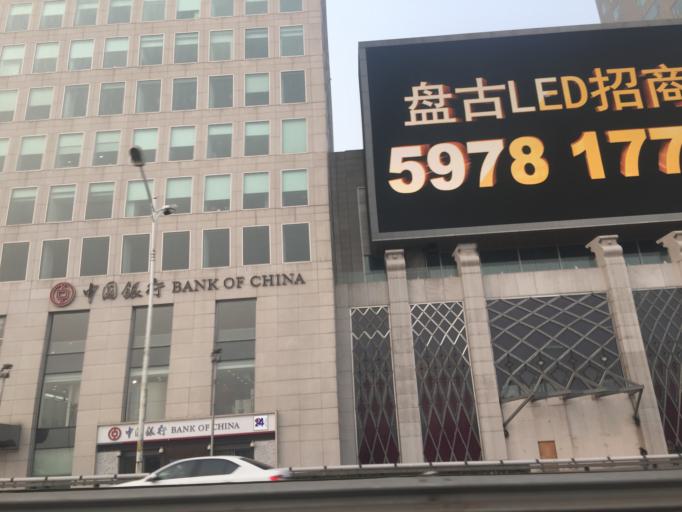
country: CN
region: Beijing
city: Datun
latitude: 39.9882
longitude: 116.3813
